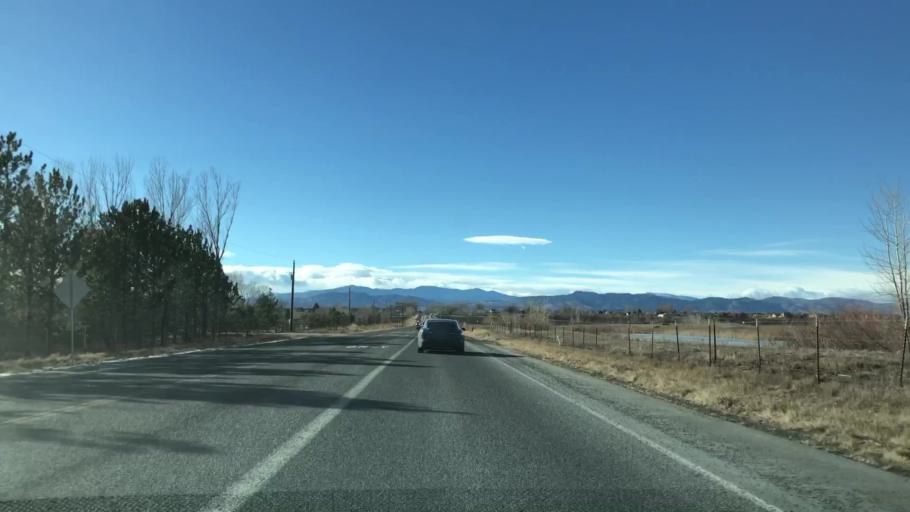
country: US
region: Colorado
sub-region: Weld County
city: Windsor
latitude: 40.5085
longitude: -104.9837
